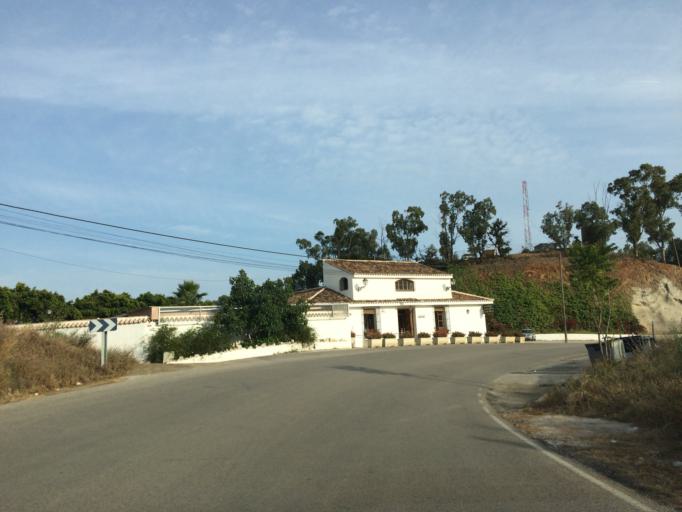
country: ES
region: Andalusia
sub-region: Provincia de Malaga
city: Malaga
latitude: 36.7494
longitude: -4.4074
